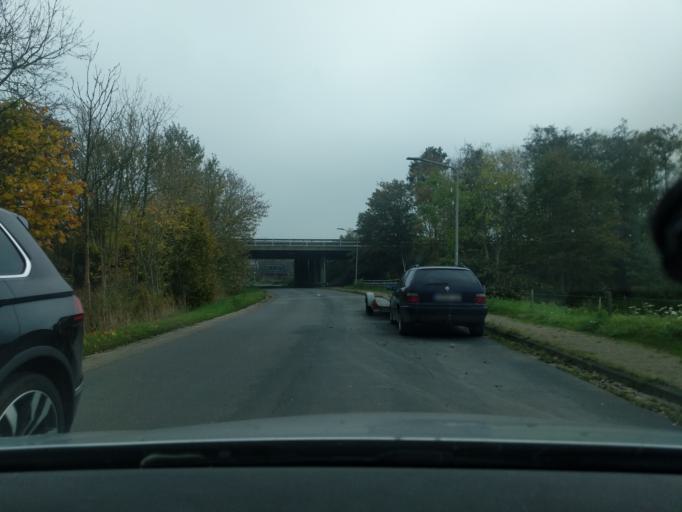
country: DE
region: Lower Saxony
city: Cuxhaven
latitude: 53.8363
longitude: 8.7280
